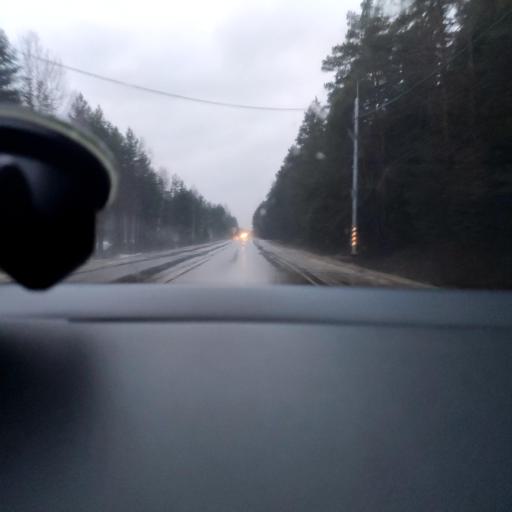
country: RU
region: Moskovskaya
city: Krasnyy Tkach
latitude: 55.4111
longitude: 39.1687
